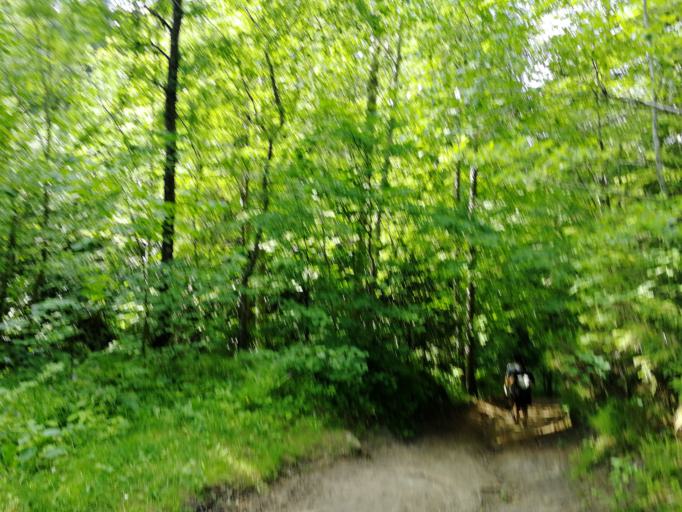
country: LV
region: Cesu Rajons
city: Cesis
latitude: 57.2995
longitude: 25.2193
